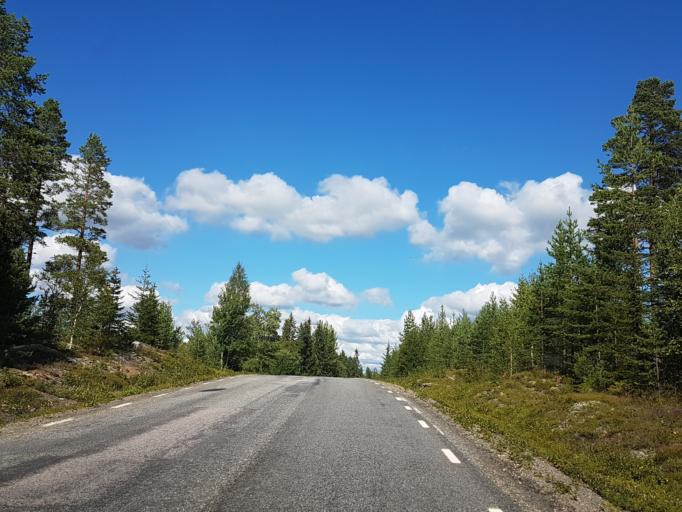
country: SE
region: Vaesterbotten
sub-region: Skelleftea Kommun
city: Burtraesk
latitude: 64.2324
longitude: 20.4728
